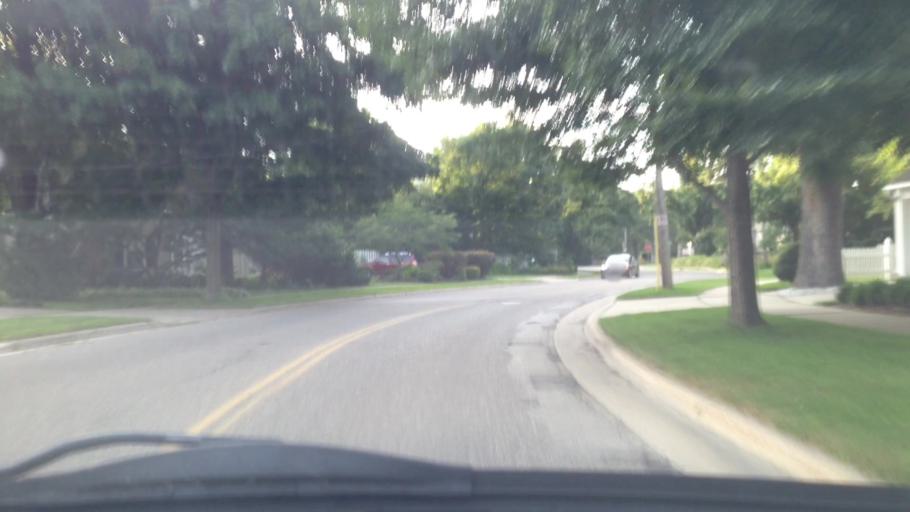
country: US
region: Minnesota
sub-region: Olmsted County
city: Rochester
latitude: 44.0097
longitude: -92.4723
